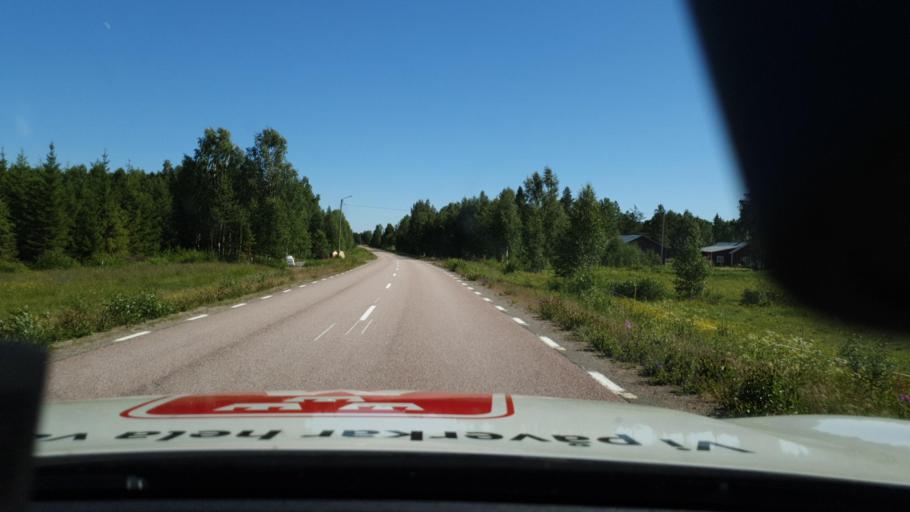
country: SE
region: Norrbotten
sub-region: Lulea Kommun
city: Ranea
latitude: 65.9592
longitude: 22.3849
